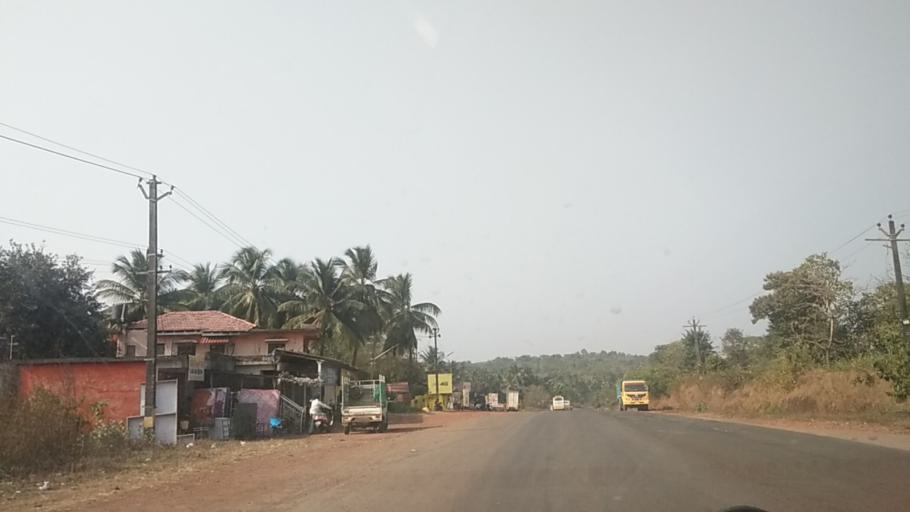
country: IN
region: Goa
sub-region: North Goa
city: Colovale
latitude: 15.6691
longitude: 73.8378
